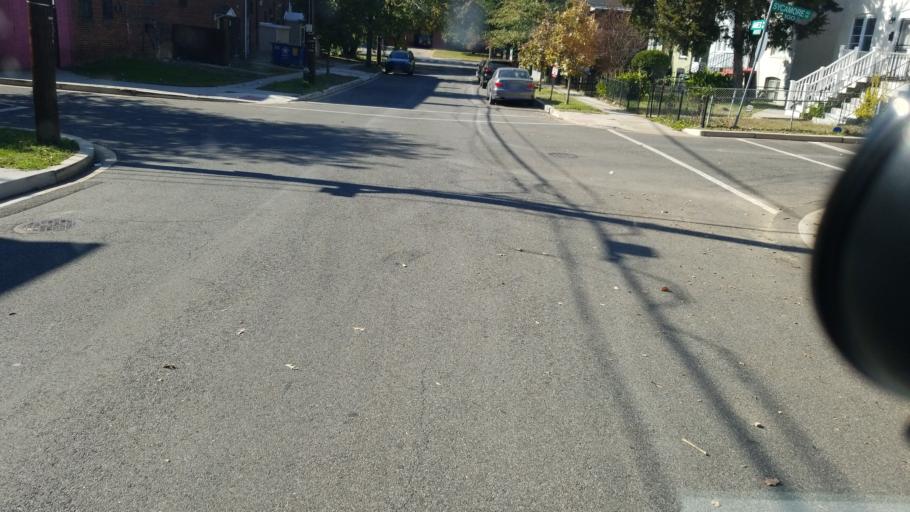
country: US
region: Maryland
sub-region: Prince George's County
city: Capitol Heights
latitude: 38.8908
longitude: -76.9316
